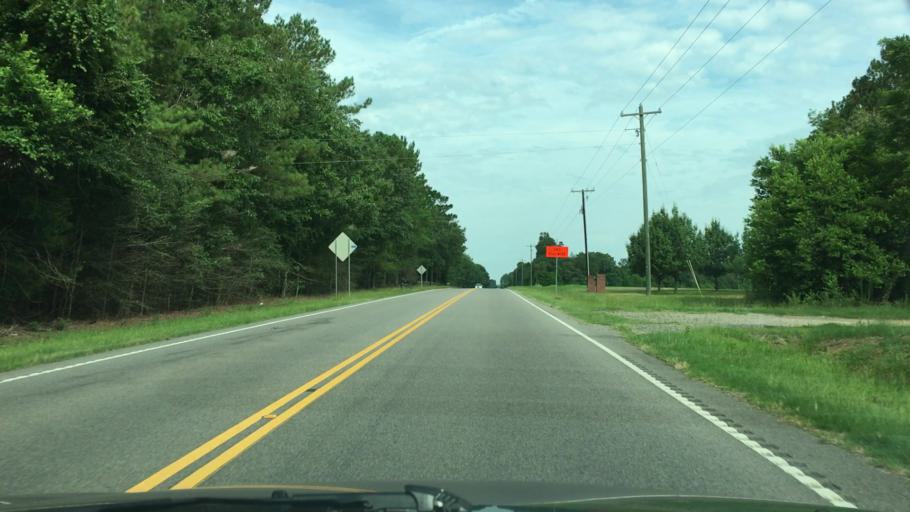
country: US
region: South Carolina
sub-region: Lexington County
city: Leesville
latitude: 33.6789
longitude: -81.4396
